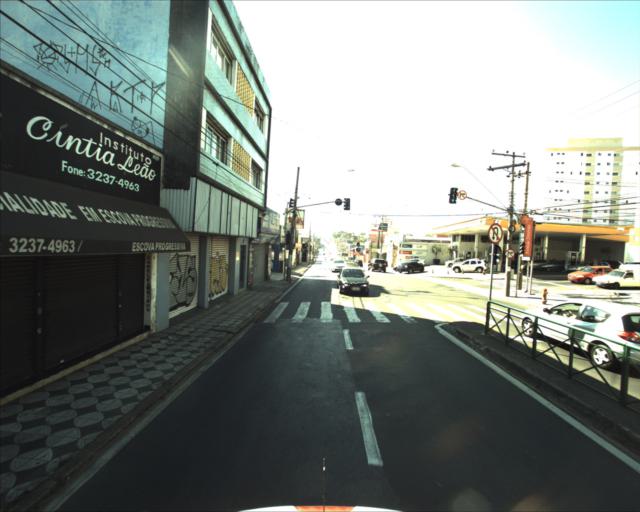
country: BR
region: Sao Paulo
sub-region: Sorocaba
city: Sorocaba
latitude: -23.5000
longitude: -47.4484
